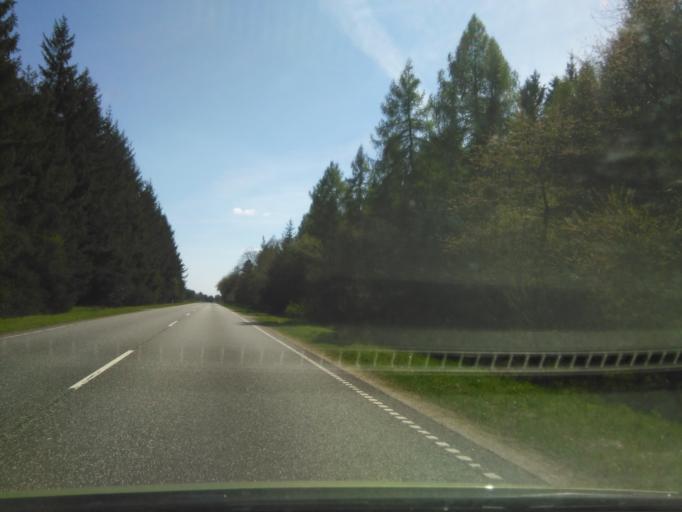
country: DK
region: Central Jutland
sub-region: Ikast-Brande Kommune
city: Bording Kirkeby
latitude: 56.2176
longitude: 9.3185
